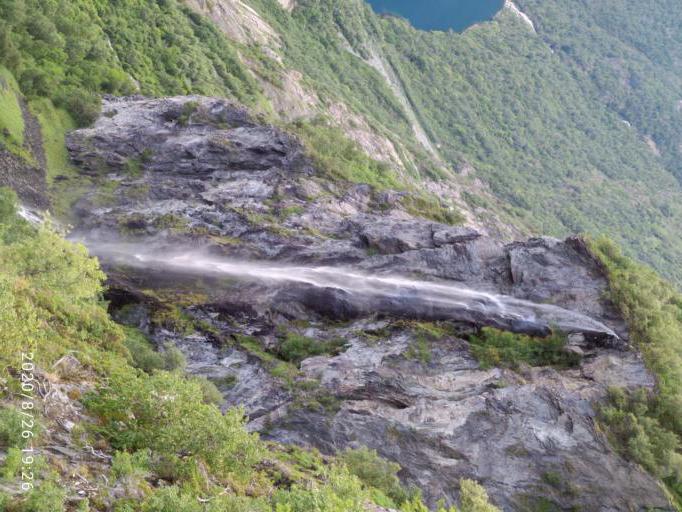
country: NO
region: More og Romsdal
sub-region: Norddal
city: Valldal
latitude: 62.1271
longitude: 7.1619
